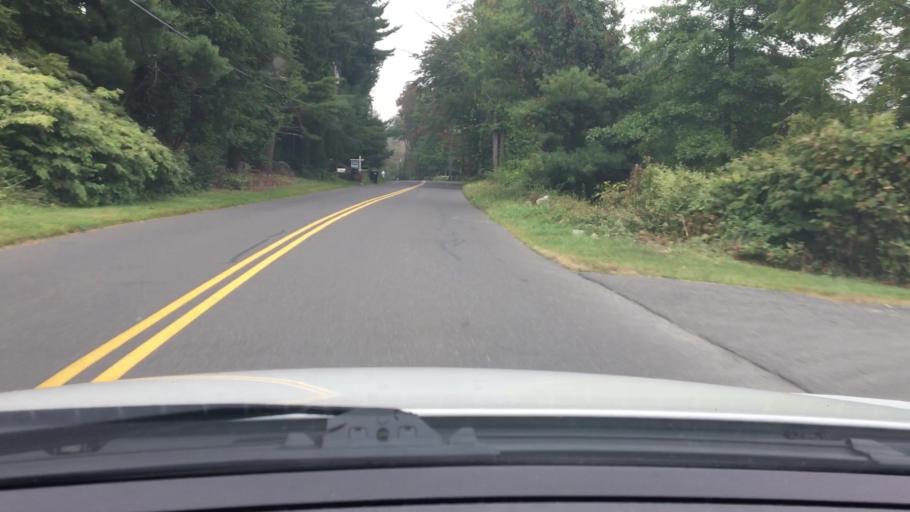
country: US
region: Connecticut
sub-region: Fairfield County
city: Newtown
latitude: 41.4601
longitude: -73.3596
